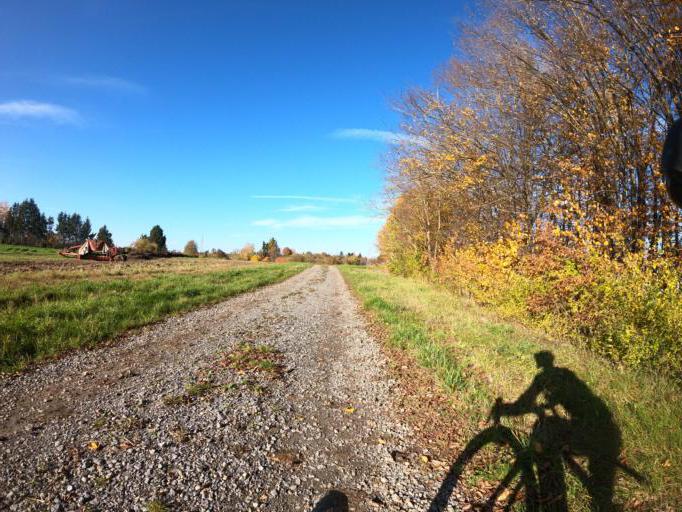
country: DE
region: Baden-Wuerttemberg
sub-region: Regierungsbezirk Stuttgart
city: Magstadt
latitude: 48.7354
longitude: 8.9671
